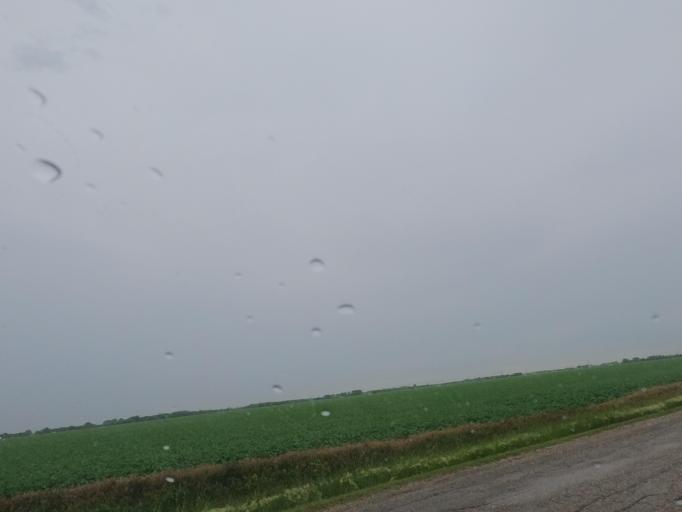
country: CA
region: Manitoba
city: Winnipeg
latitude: 49.8268
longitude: -96.9812
